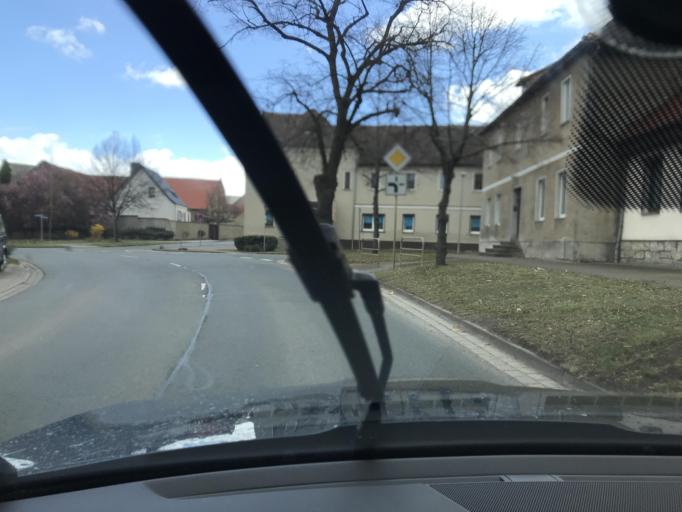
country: DE
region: Saxony-Anhalt
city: Hoym
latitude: 51.7823
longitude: 11.3107
